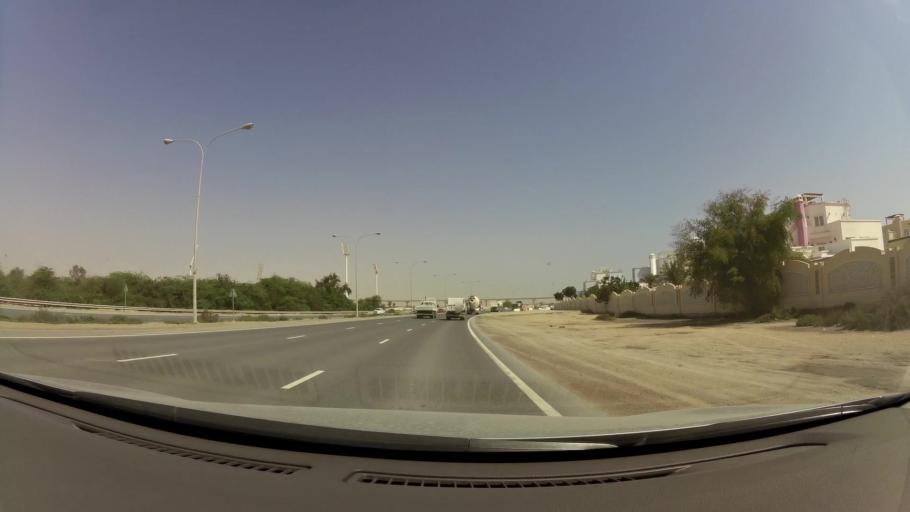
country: QA
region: Baladiyat ad Dawhah
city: Doha
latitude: 25.3719
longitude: 51.4972
